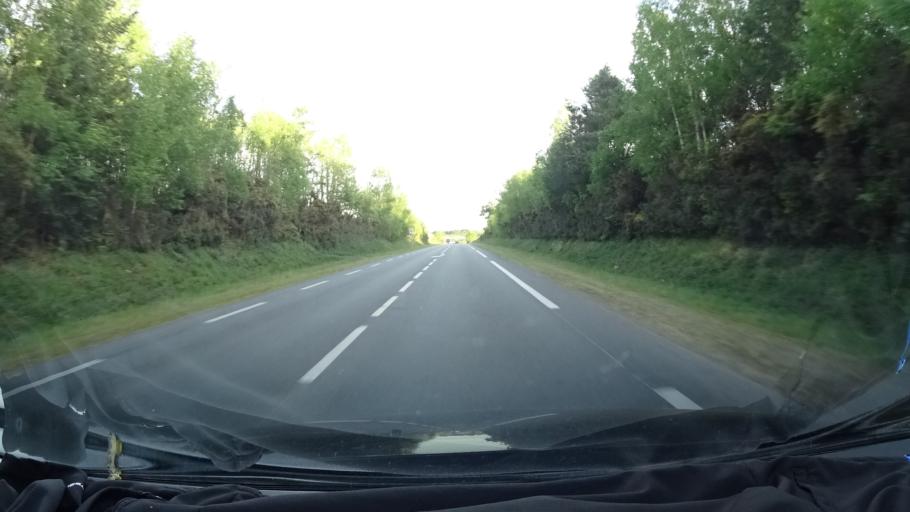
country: FR
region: Brittany
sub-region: Departement du Morbihan
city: Questembert
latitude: 47.6452
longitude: -2.4271
